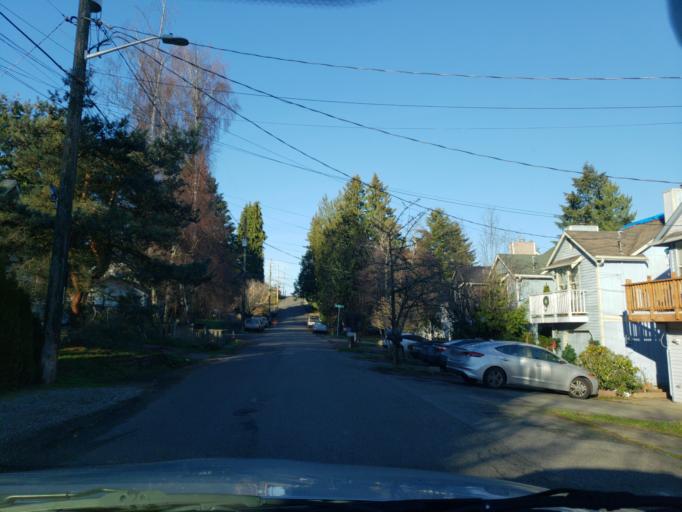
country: US
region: Washington
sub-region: King County
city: Lake Forest Park
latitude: 47.6953
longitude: -122.3068
